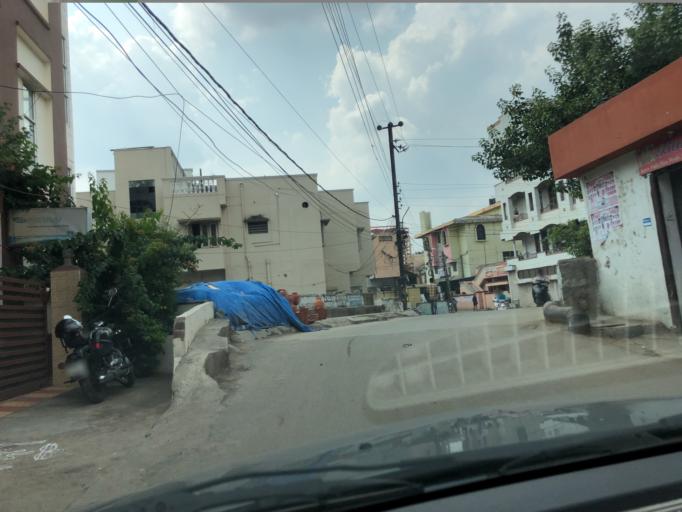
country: IN
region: Telangana
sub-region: Hyderabad
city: Malkajgiri
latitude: 17.4461
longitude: 78.4811
